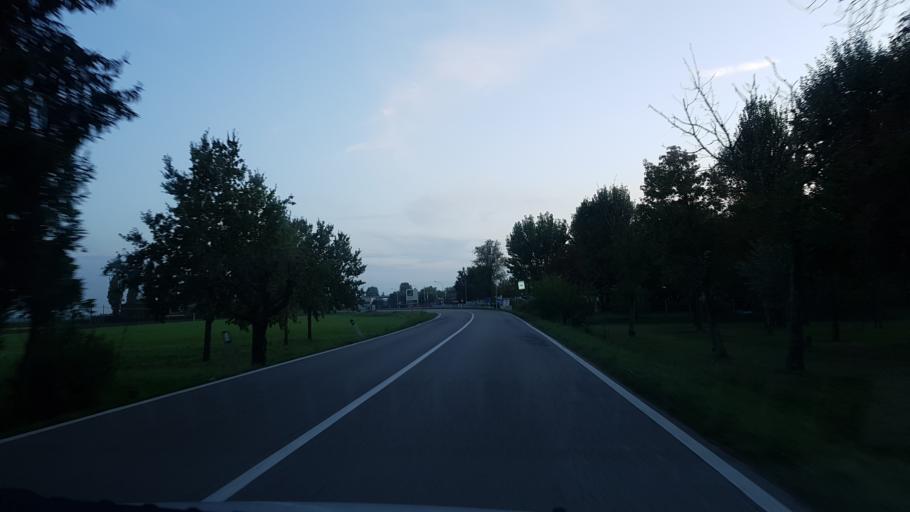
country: IT
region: Emilia-Romagna
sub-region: Provincia di Modena
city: San Prospero
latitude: 44.8114
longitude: 11.0313
